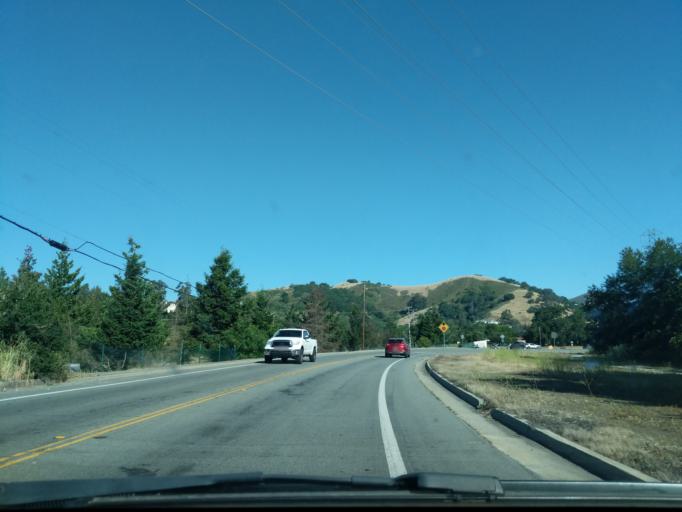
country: US
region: California
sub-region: Santa Clara County
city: San Martin
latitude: 37.0928
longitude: -121.6450
